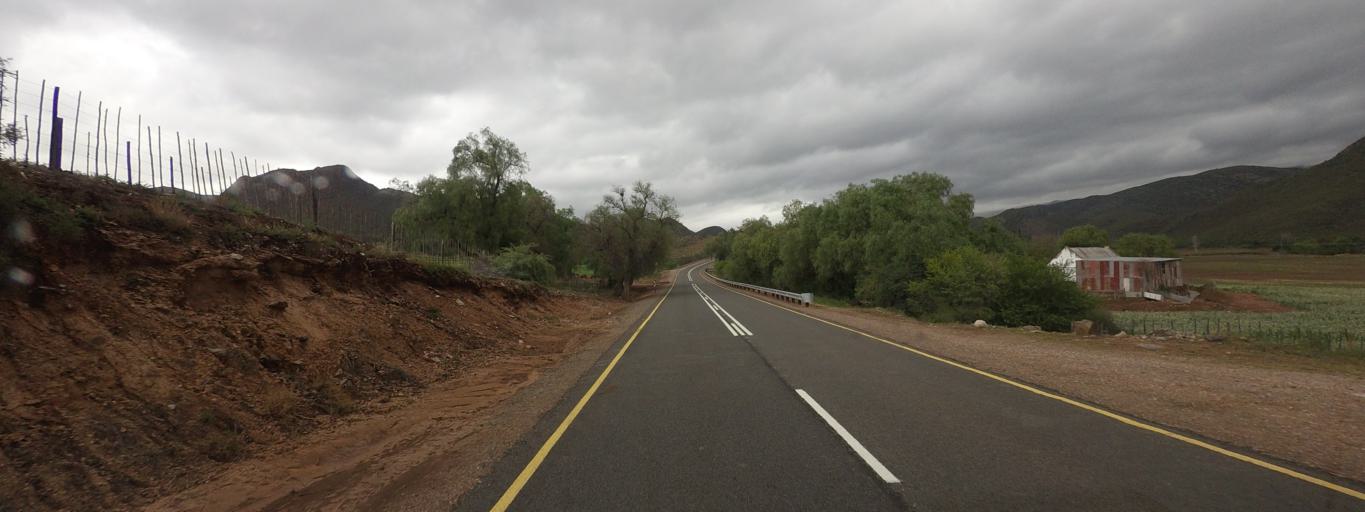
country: ZA
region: Western Cape
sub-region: Eden District Municipality
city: Oudtshoorn
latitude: -33.4069
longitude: 22.2266
